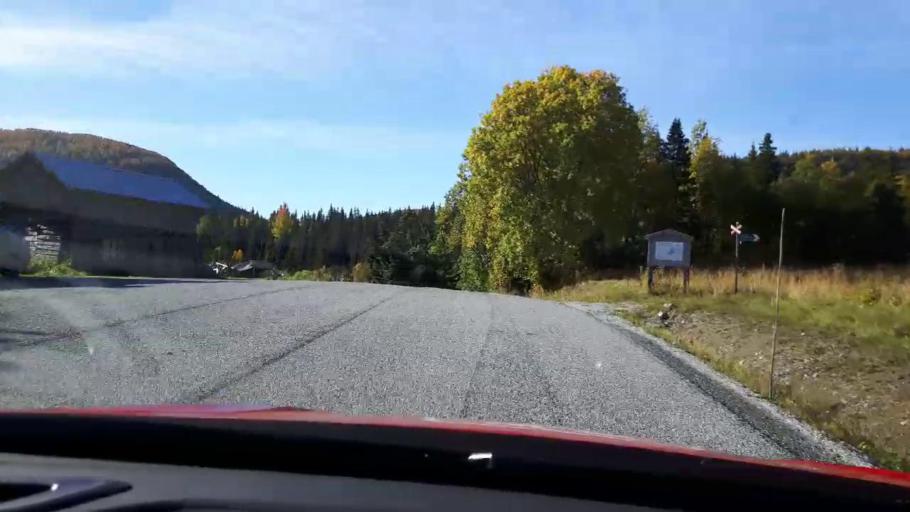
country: NO
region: Nord-Trondelag
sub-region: Royrvik
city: Royrvik
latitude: 64.7293
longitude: 13.9429
